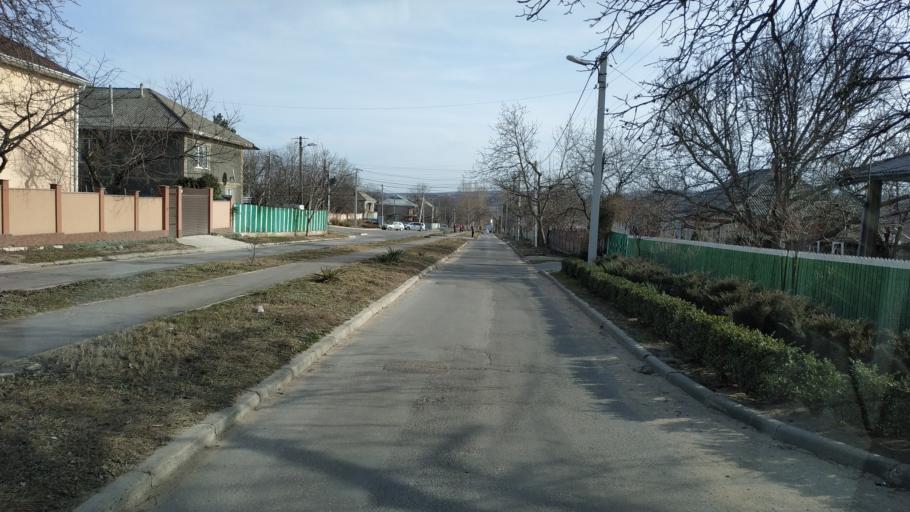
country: MD
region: Chisinau
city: Vatra
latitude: 47.0752
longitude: 28.6921
